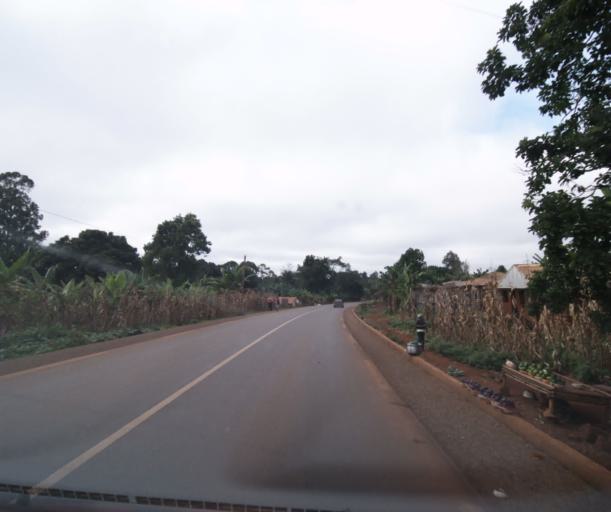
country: CM
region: West
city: Mbouda
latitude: 5.5866
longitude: 10.2972
